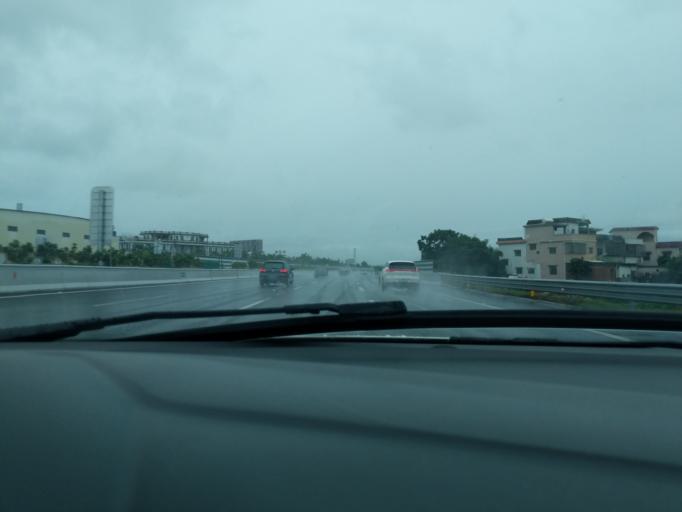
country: CN
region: Guangdong
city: Shuikou
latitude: 22.4816
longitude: 112.7742
